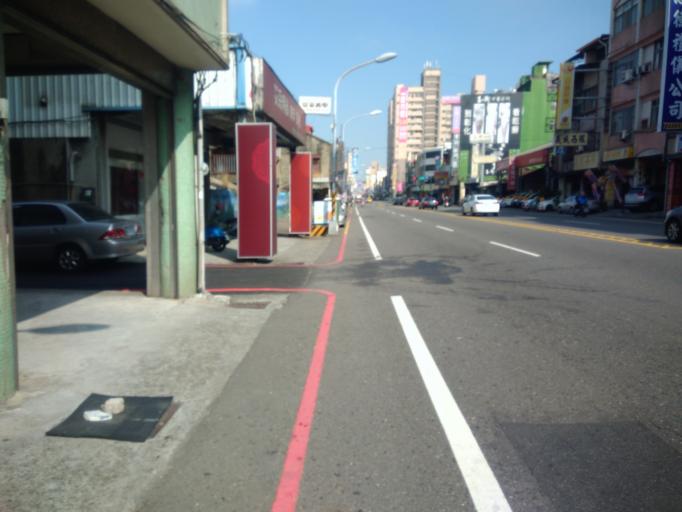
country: TW
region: Taiwan
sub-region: Changhua
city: Chang-hua
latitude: 24.0848
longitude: 120.5550
